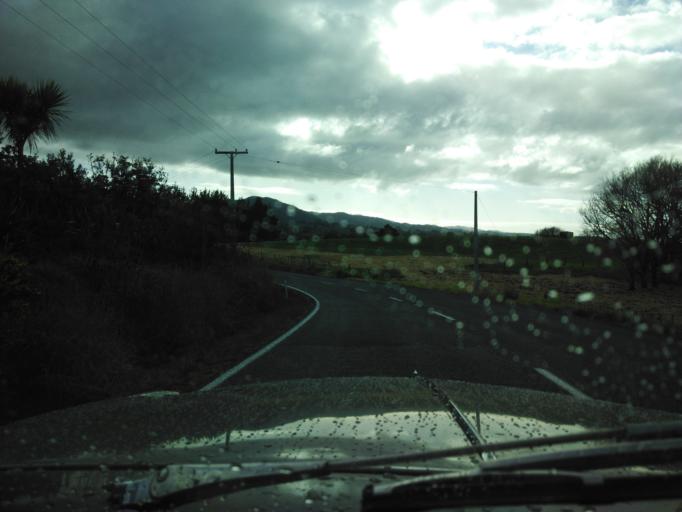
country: NZ
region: Auckland
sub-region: Auckland
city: Wellsford
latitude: -36.1748
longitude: 174.4165
